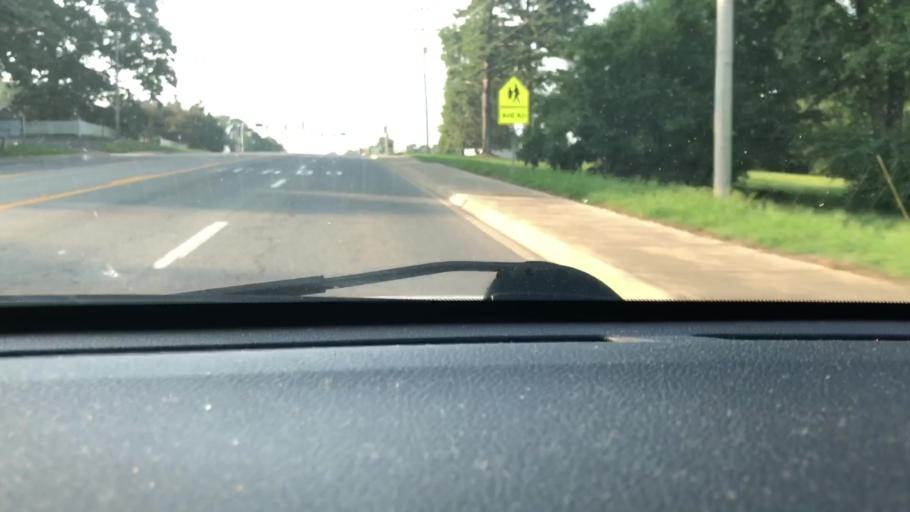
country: US
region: Arkansas
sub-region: Saline County
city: Bryant
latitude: 34.6043
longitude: -92.4912
